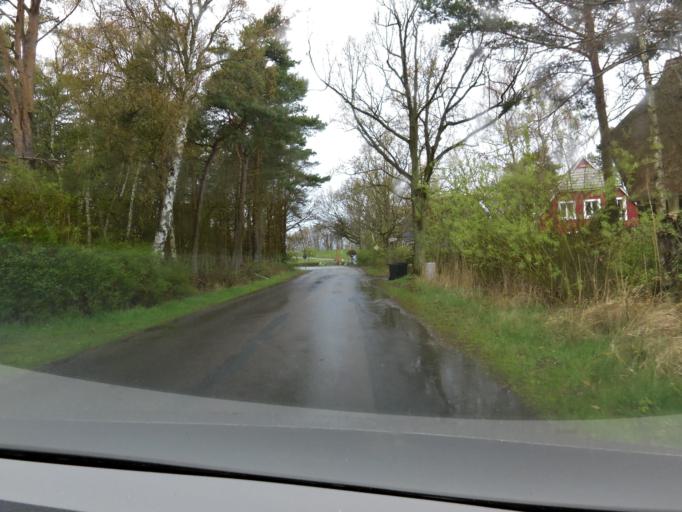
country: DE
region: Mecklenburg-Vorpommern
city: Zingst
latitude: 54.4402
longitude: 12.7219
